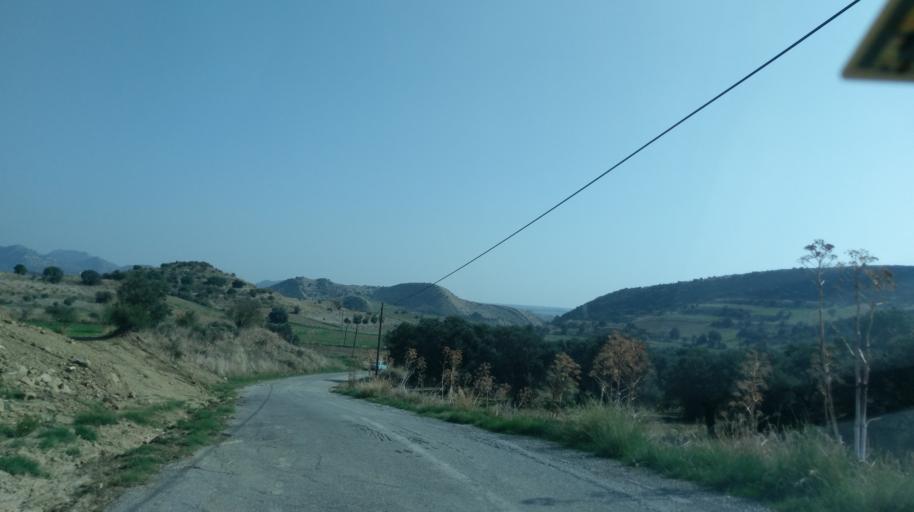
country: CY
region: Ammochostos
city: Lefkonoiko
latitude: 35.3293
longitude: 33.6977
